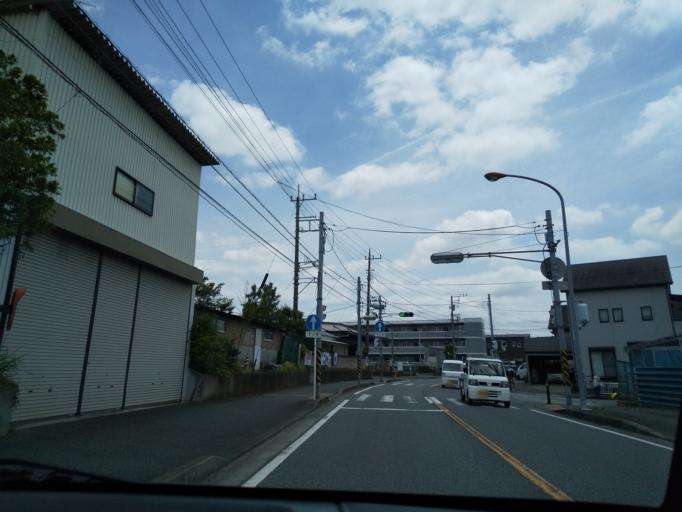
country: JP
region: Tokyo
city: Hachioji
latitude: 35.5696
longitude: 139.3466
